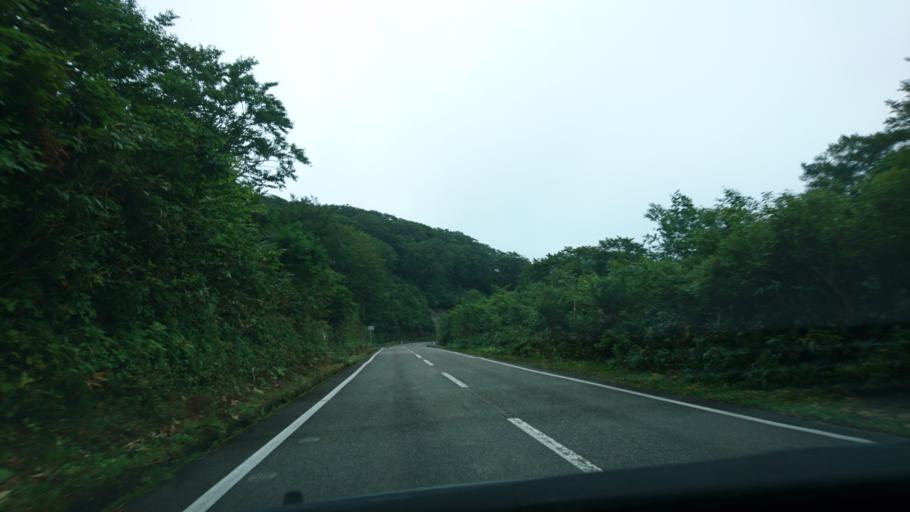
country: JP
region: Akita
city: Yuzawa
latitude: 38.9764
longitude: 140.7497
